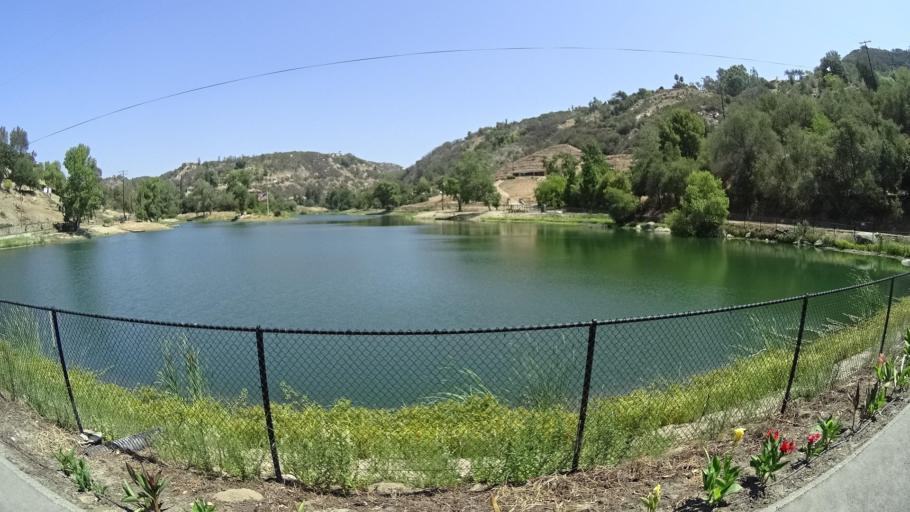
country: US
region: California
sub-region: San Diego County
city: Fallbrook
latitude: 33.4392
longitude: -117.2870
